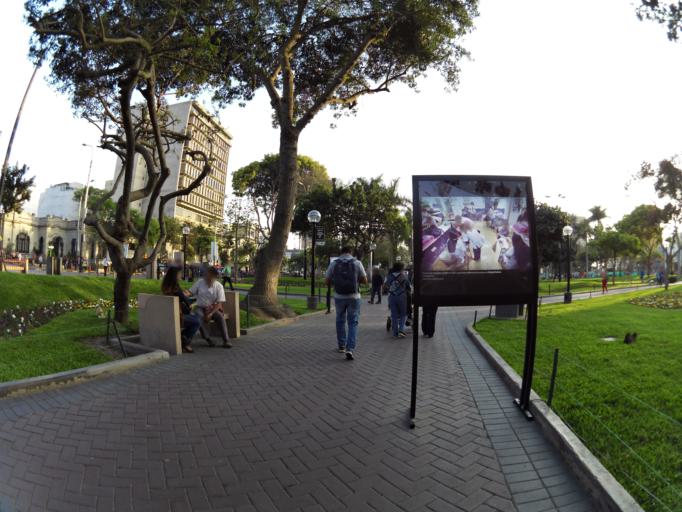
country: PE
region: Lima
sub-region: Lima
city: San Isidro
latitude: -12.1202
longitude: -77.0293
